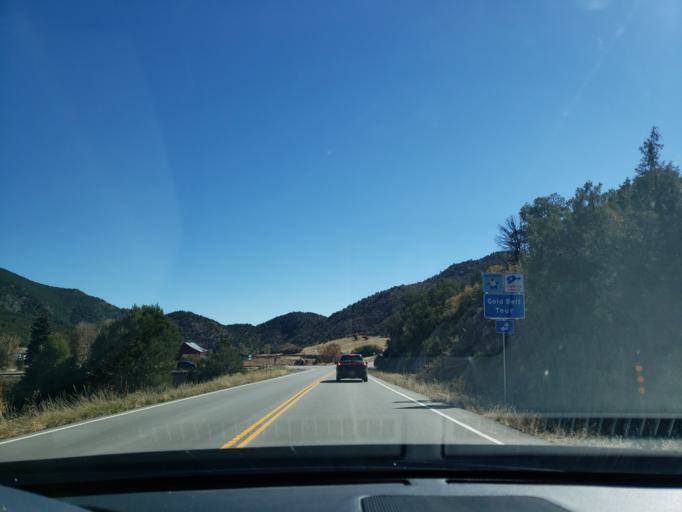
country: US
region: Colorado
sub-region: Fremont County
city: Canon City
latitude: 38.5862
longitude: -105.4192
